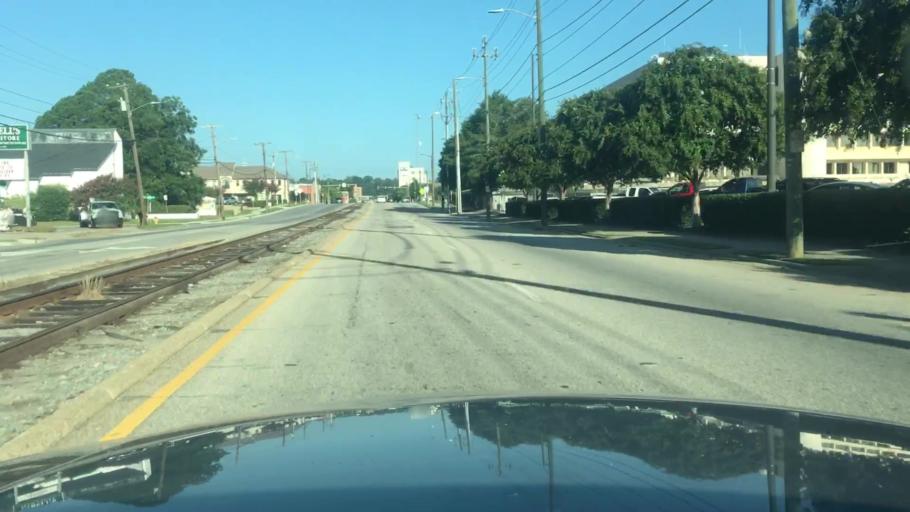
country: US
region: North Carolina
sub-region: Cumberland County
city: Fayetteville
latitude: 35.0494
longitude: -78.8756
